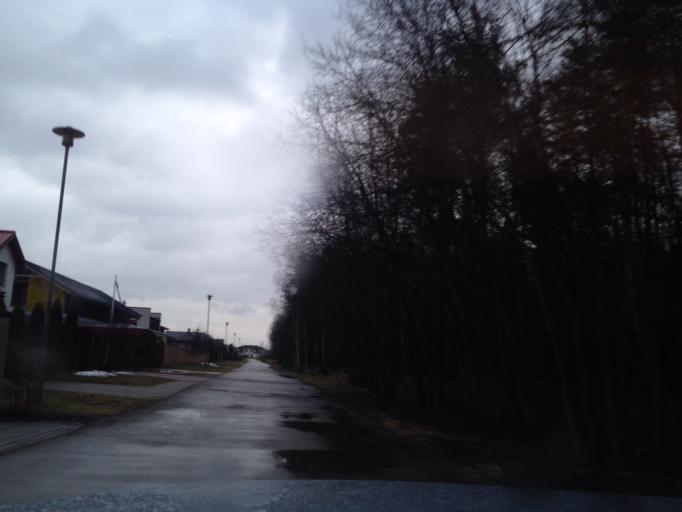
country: LV
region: Marupe
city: Marupe
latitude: 56.8880
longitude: 24.0287
